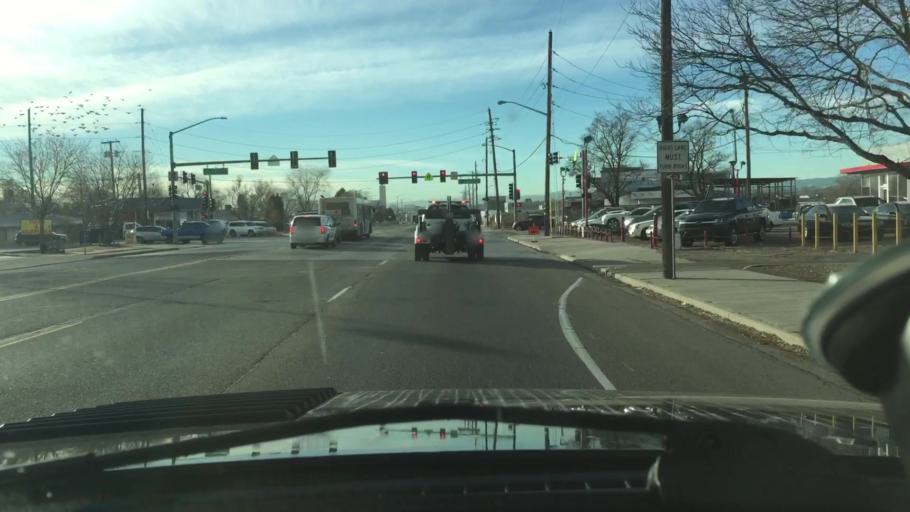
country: US
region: Colorado
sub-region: Adams County
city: Twin Lakes
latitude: 39.8244
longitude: -105.0063
